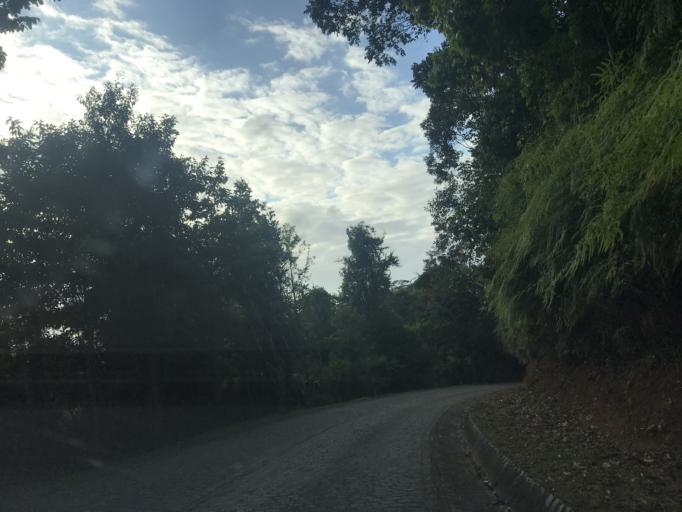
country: BR
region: Bahia
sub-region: Gandu
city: Gandu
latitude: -13.9092
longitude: -39.4653
